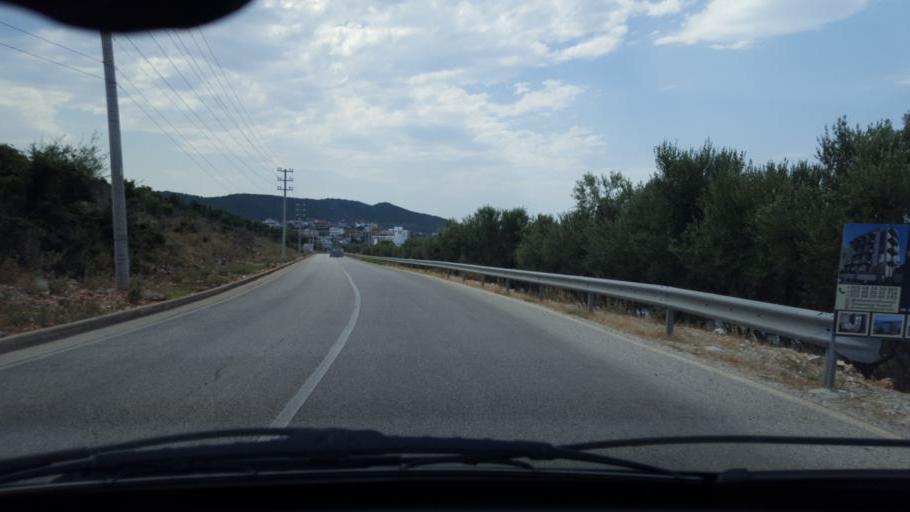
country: AL
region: Vlore
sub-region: Rrethi i Sarandes
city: Xarre
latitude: 39.7834
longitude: 20.0071
